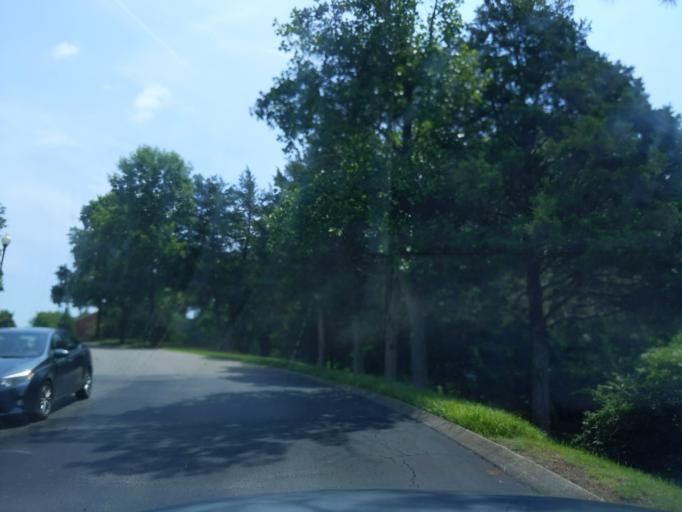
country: US
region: Tennessee
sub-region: Williamson County
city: Brentwood Estates
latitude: 36.0426
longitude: -86.7422
